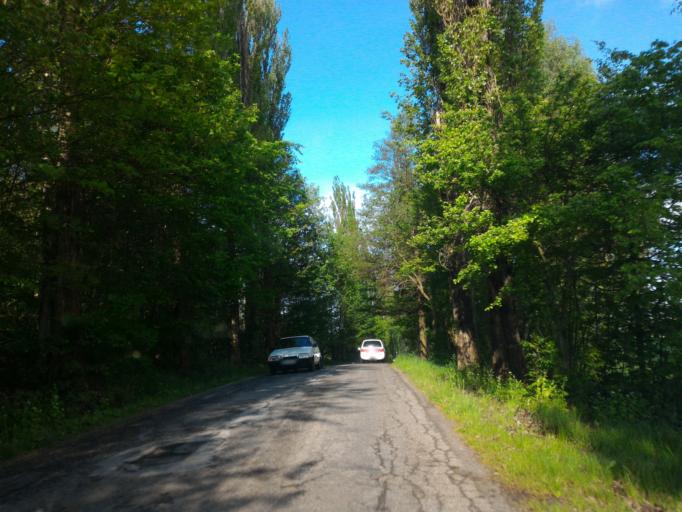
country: CZ
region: Vysocina
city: Ledec nad Sazavou
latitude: 49.6520
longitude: 15.2878
